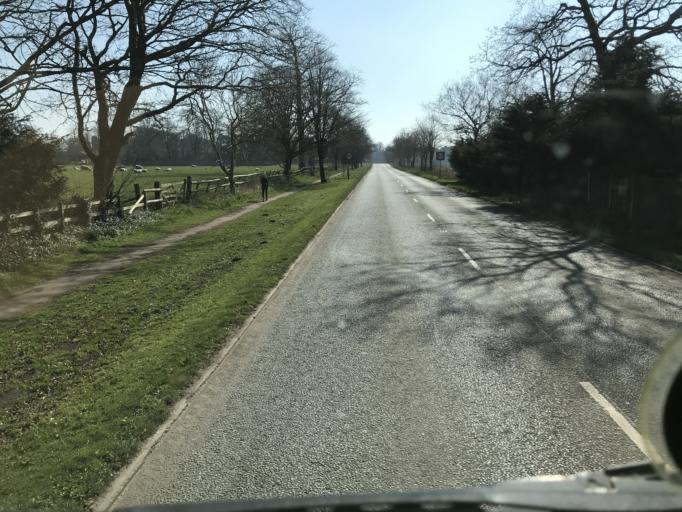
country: GB
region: England
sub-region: Cheshire East
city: Knutsford
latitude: 53.2936
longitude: -2.3541
